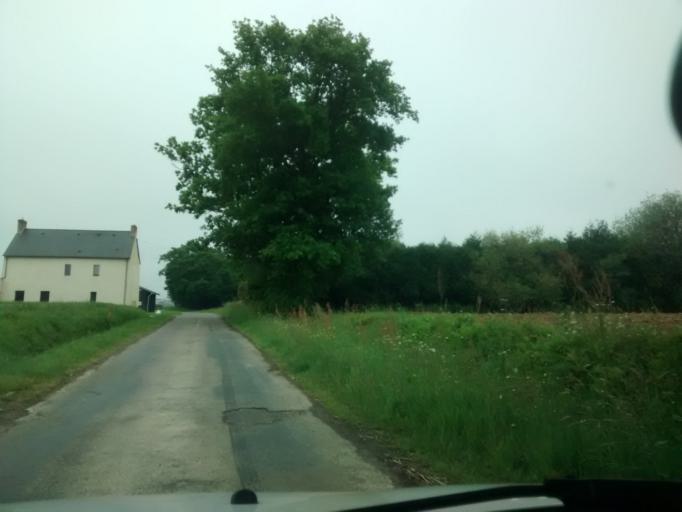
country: FR
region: Brittany
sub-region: Departement d'Ille-et-Vilaine
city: Montgermont
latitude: 48.1426
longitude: -1.7081
